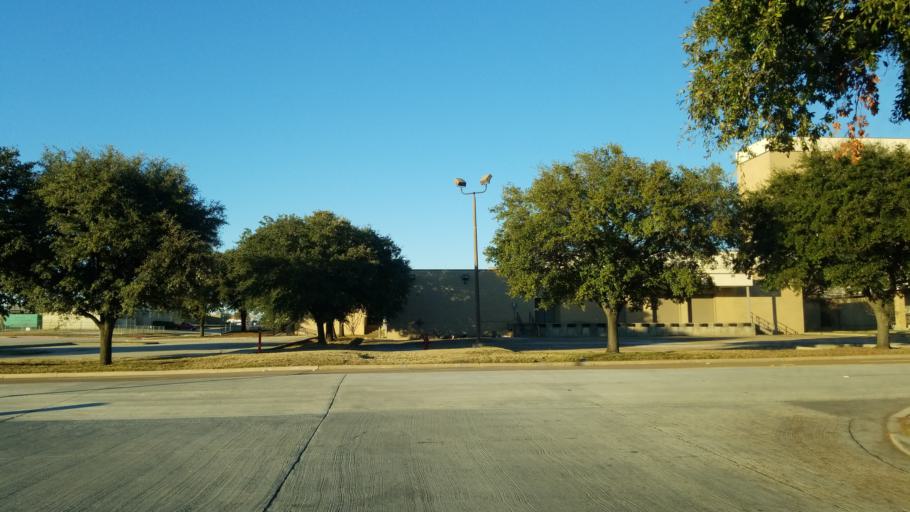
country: US
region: Texas
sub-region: Dallas County
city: Grand Prairie
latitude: 32.7318
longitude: -97.0500
